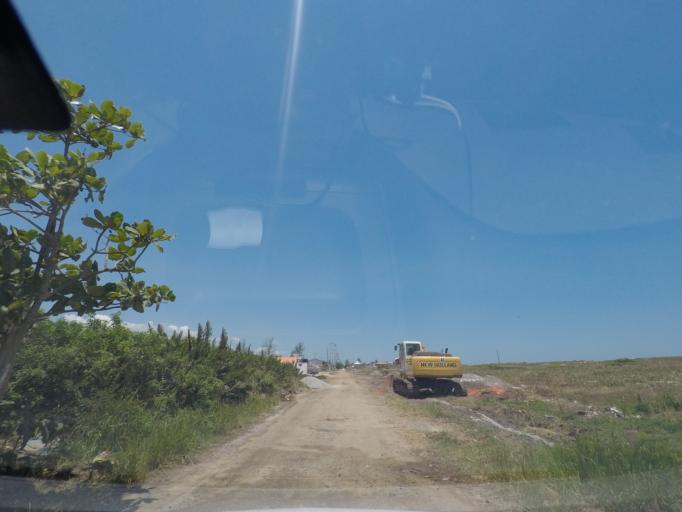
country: BR
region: Rio de Janeiro
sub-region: Niteroi
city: Niteroi
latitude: -22.9684
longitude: -42.9732
